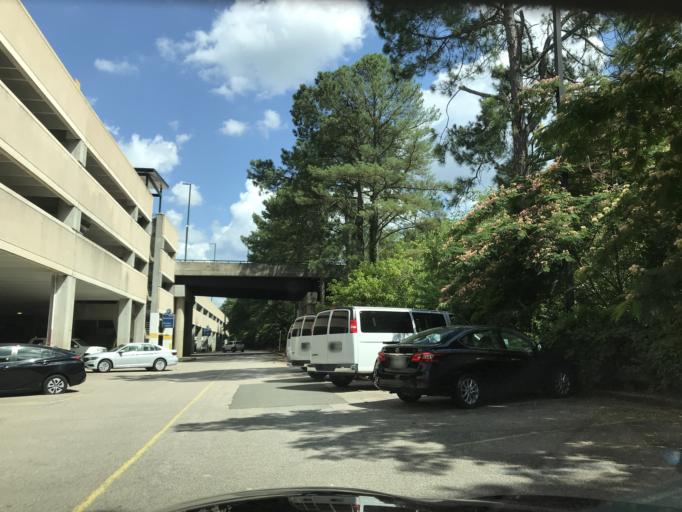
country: US
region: North Carolina
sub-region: Wake County
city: West Raleigh
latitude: 35.8400
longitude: -78.6817
